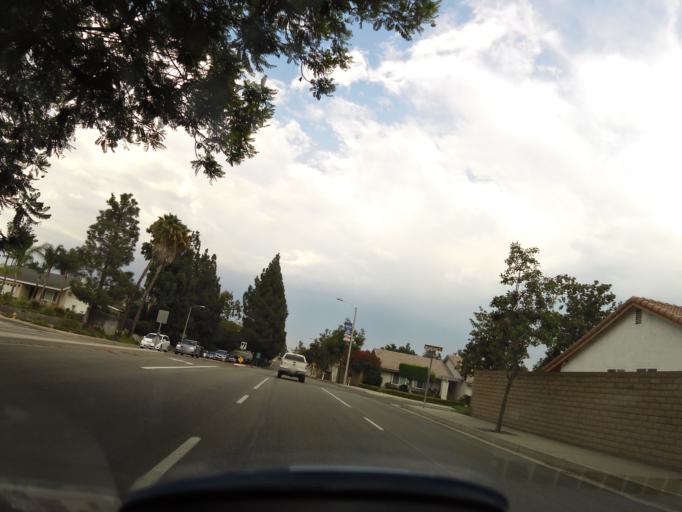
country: US
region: California
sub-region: Orange County
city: Yorba Linda
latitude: 33.8884
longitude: -117.8233
